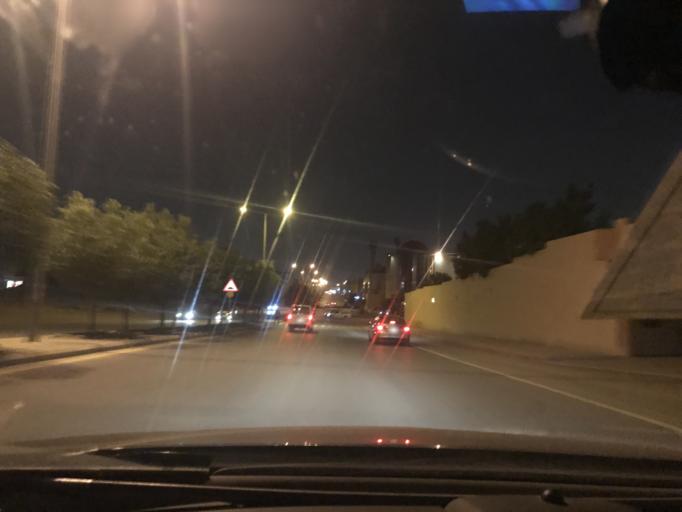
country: SA
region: Ar Riyad
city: Riyadh
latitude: 24.7527
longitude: 46.7544
